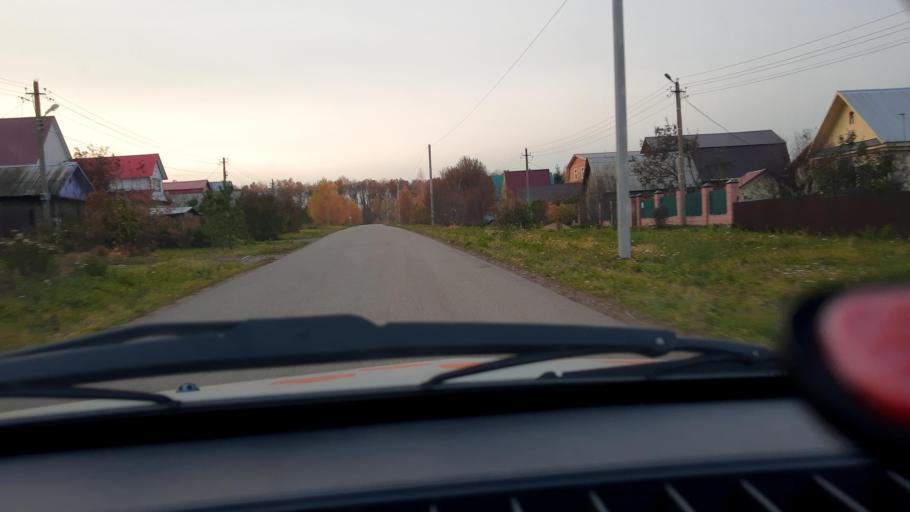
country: RU
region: Bashkortostan
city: Iglino
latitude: 54.7951
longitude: 56.3160
